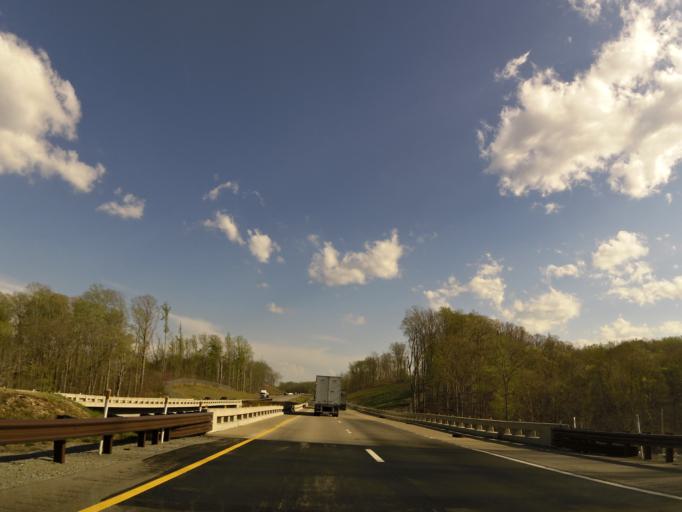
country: US
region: Tennessee
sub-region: Williamson County
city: Fairview
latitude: 35.8396
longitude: -87.0625
